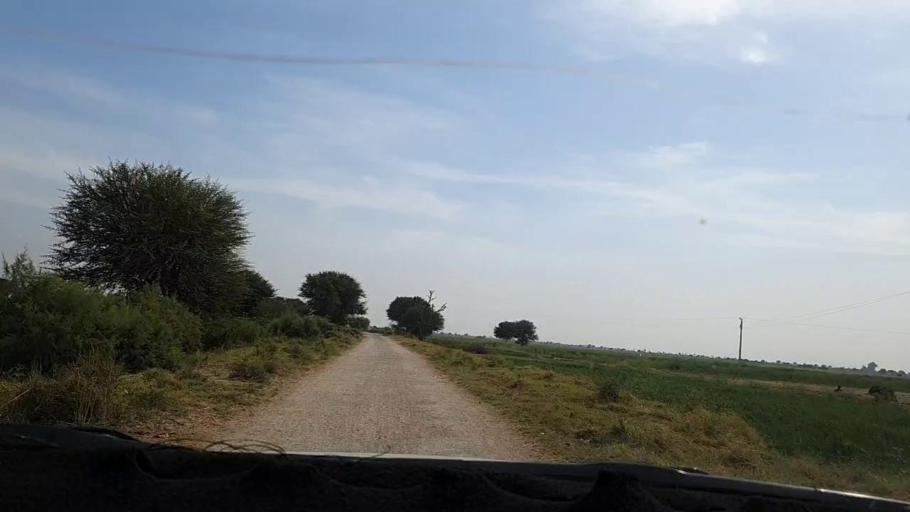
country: PK
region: Sindh
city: Pithoro
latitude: 25.5496
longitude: 69.3293
